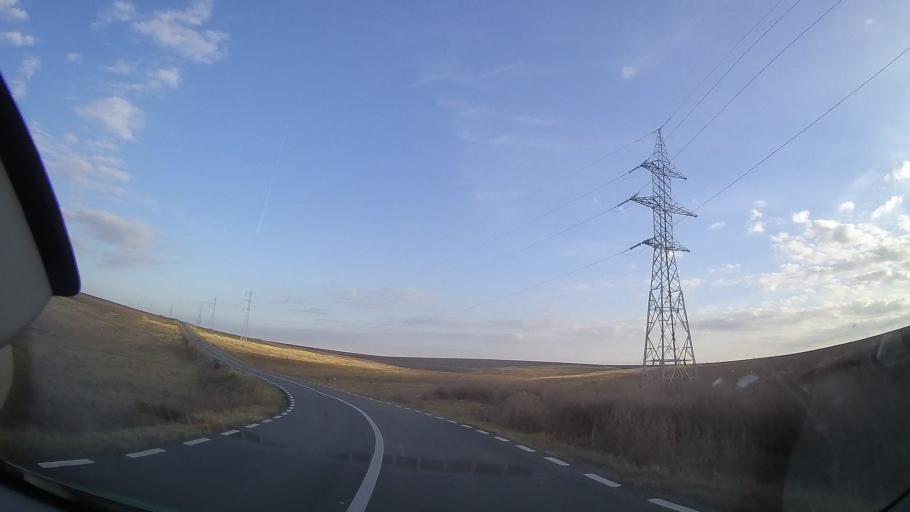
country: RO
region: Constanta
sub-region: Comuna Chirnogeni
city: Plopeni
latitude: 43.9543
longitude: 28.1508
